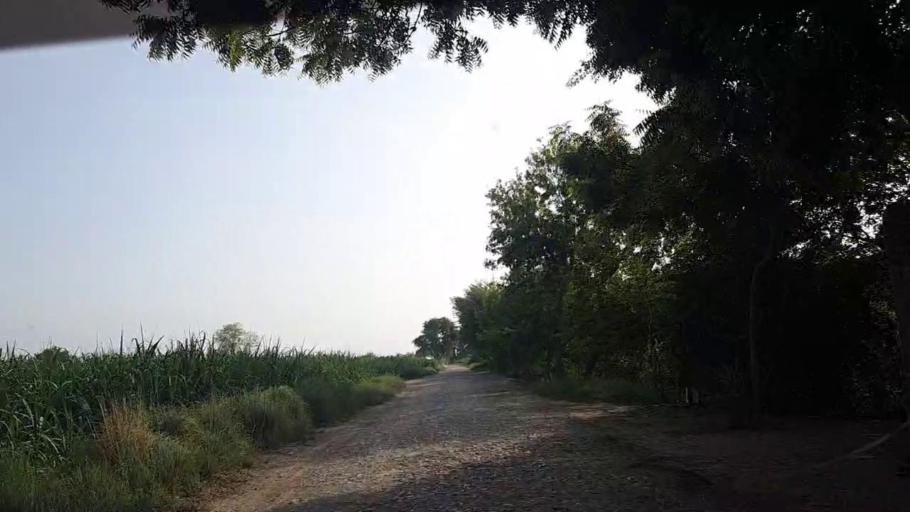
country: PK
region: Sindh
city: Ghotki
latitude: 27.9929
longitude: 69.2650
